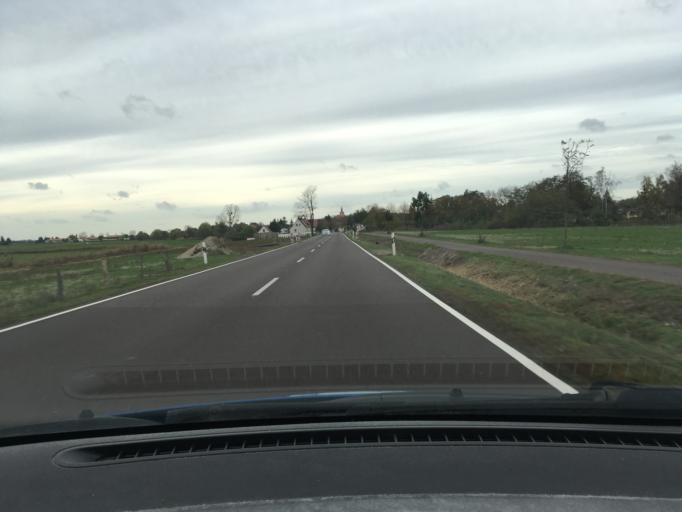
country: DE
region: Saxony-Anhalt
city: Wahlitz
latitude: 52.1141
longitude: 11.7732
